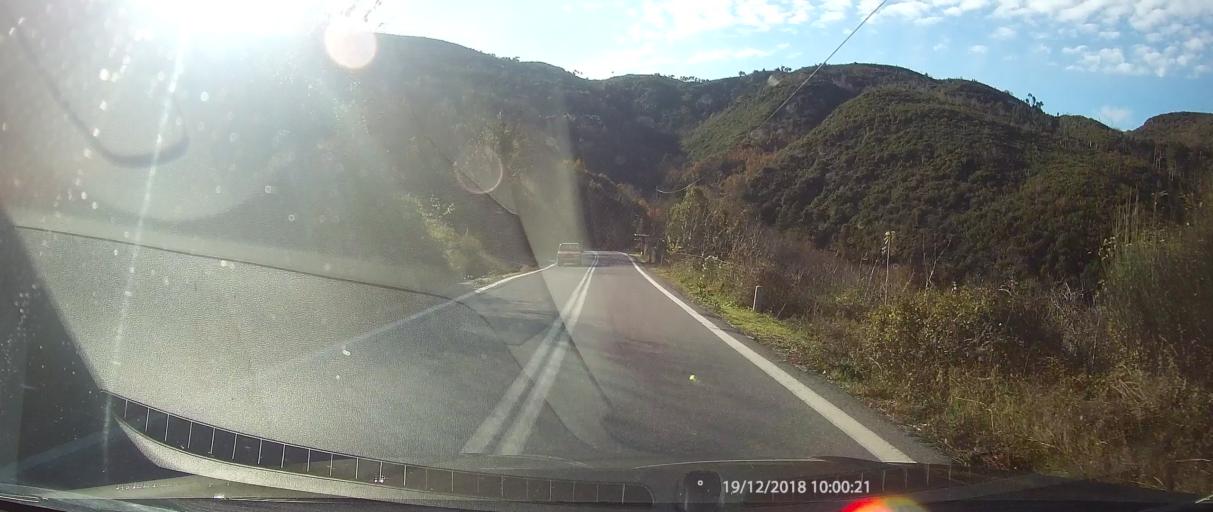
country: GR
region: Peloponnese
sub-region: Nomos Messinias
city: Paralia Vergas
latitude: 37.0953
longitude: 22.2351
